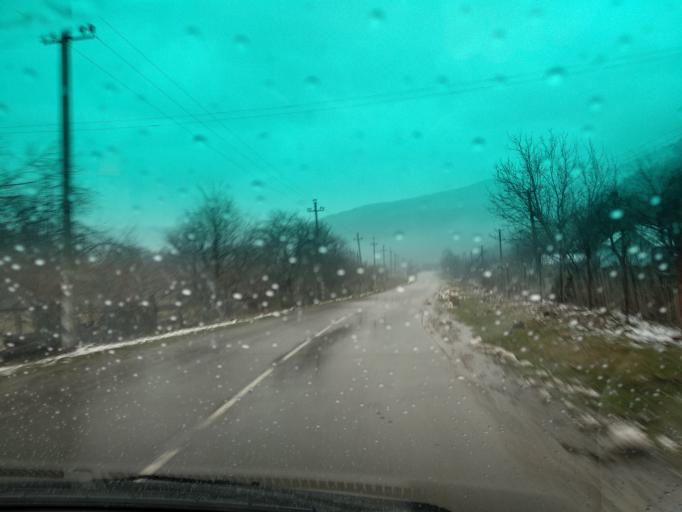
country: RU
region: Krasnodarskiy
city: Khadyzhensk
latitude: 44.2366
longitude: 39.3795
